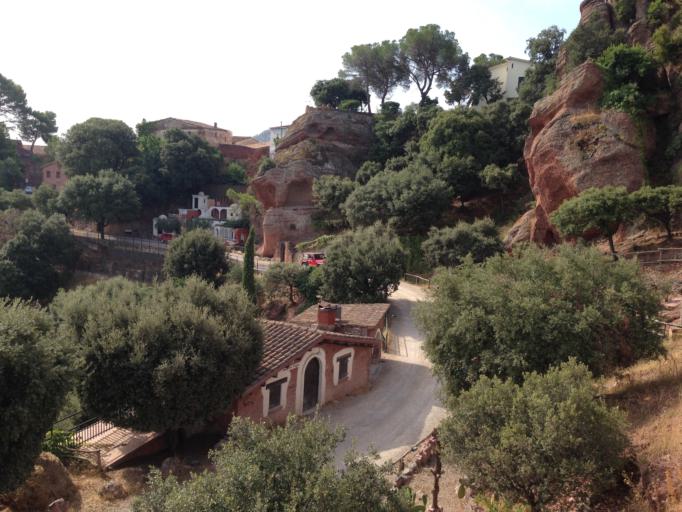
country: ES
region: Catalonia
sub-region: Provincia de Barcelona
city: Corbera de Llobregat
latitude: 41.4189
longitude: 1.9208
